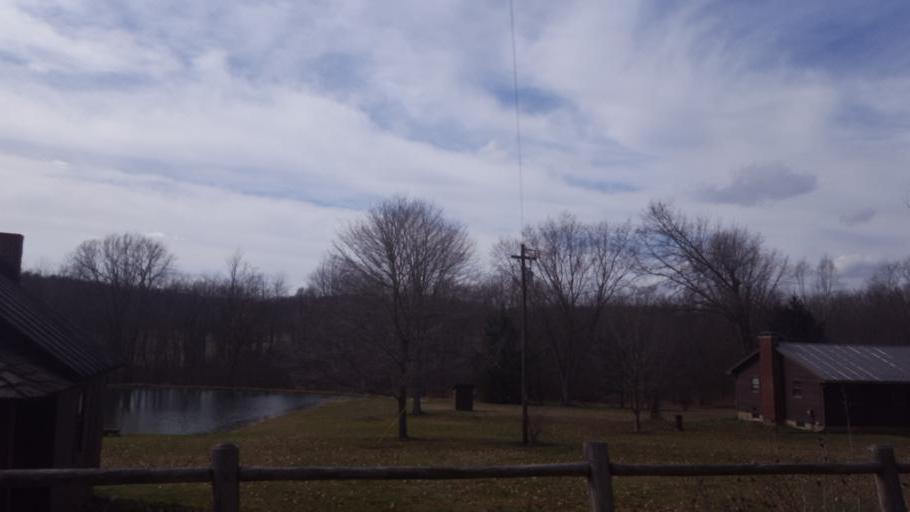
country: US
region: Ohio
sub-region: Knox County
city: Mount Vernon
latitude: 40.4508
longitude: -82.4482
